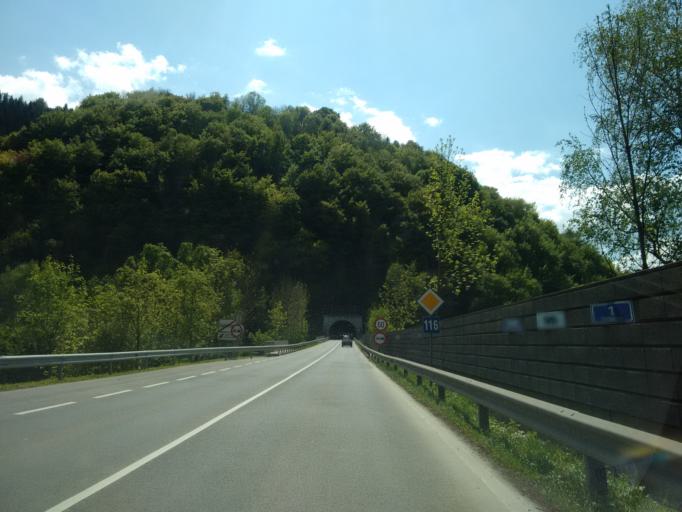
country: AT
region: Styria
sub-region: Politischer Bezirk Bruck-Muerzzuschlag
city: Kapfenberg
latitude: 47.4433
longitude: 15.2942
